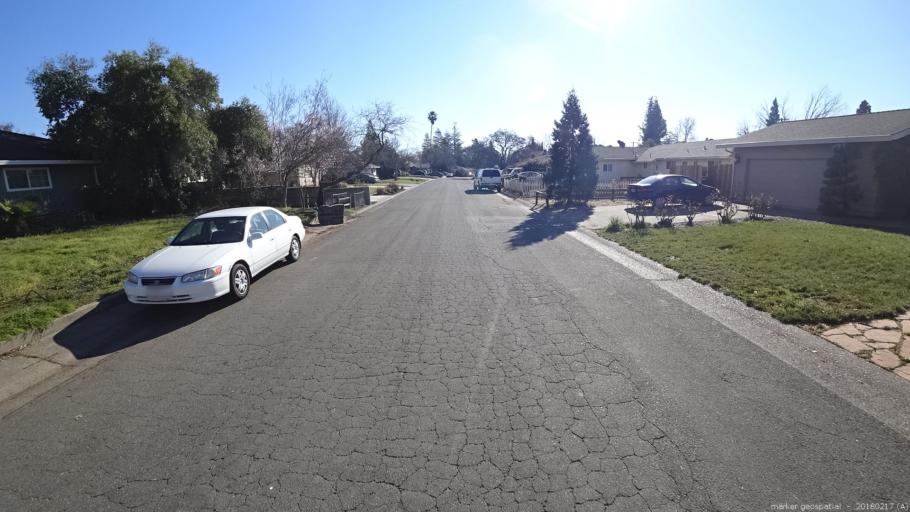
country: US
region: California
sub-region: Sacramento County
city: Folsom
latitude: 38.6659
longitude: -121.1990
